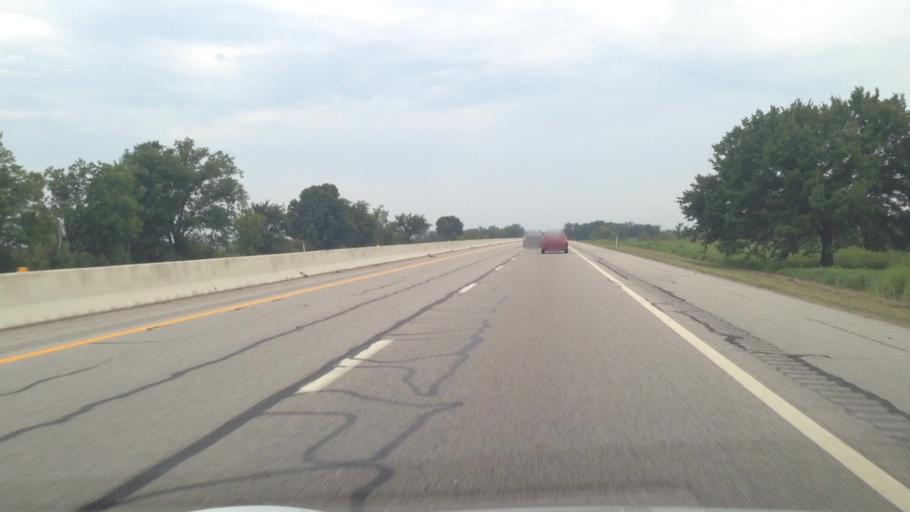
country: US
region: Oklahoma
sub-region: Ottawa County
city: Fairland
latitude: 36.7655
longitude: -94.8969
